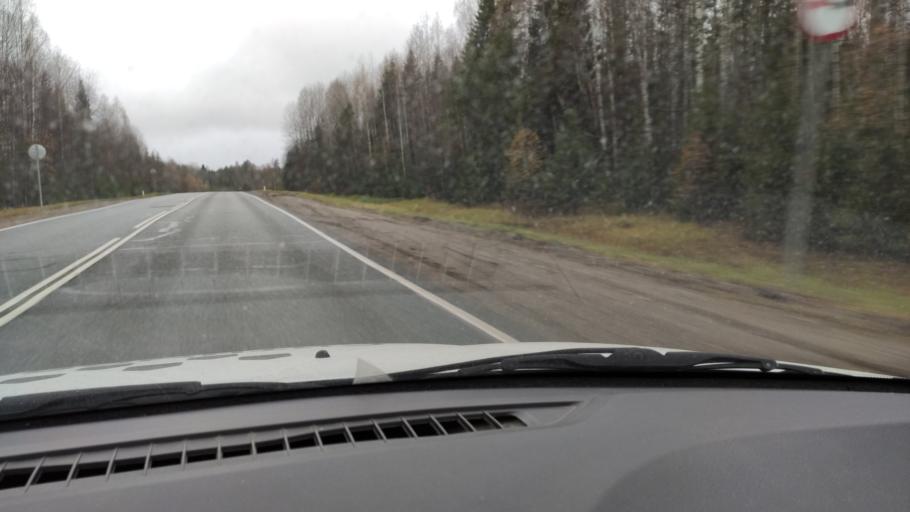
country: RU
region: Kirov
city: Chernaya Kholunitsa
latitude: 58.8913
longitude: 51.3468
